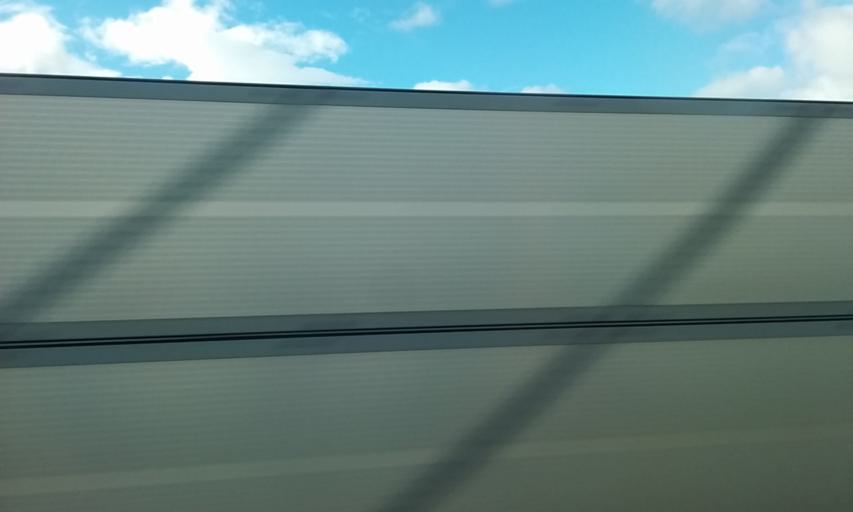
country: JP
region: Shiga Prefecture
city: Kusatsu
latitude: 35.0162
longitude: 135.9772
